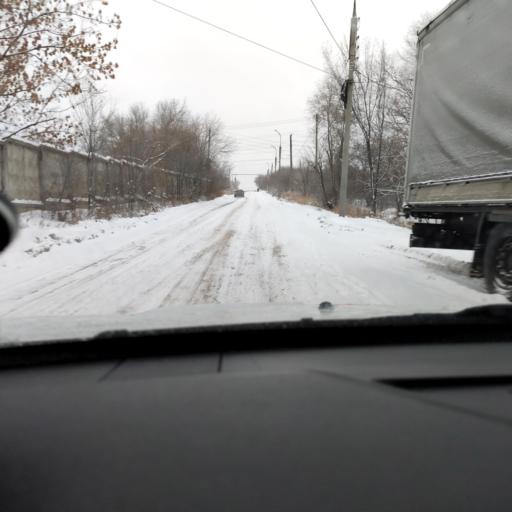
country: RU
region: Samara
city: Smyshlyayevka
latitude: 53.2377
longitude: 50.4805
